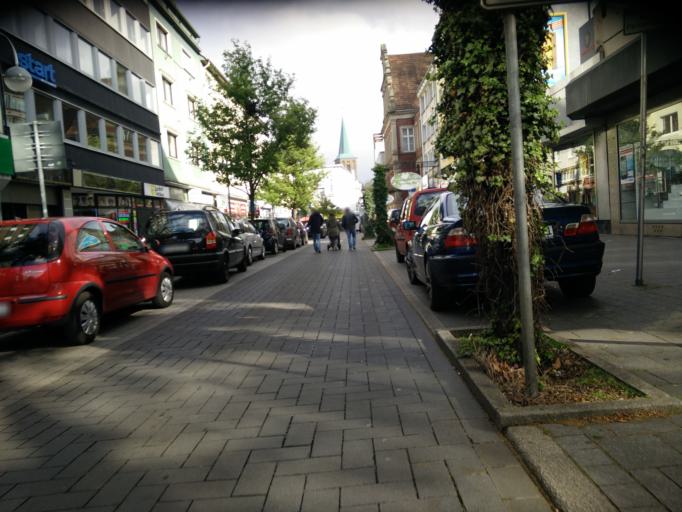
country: DE
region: North Rhine-Westphalia
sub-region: Regierungsbezirk Arnsberg
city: Bochum
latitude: 51.4845
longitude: 7.2161
